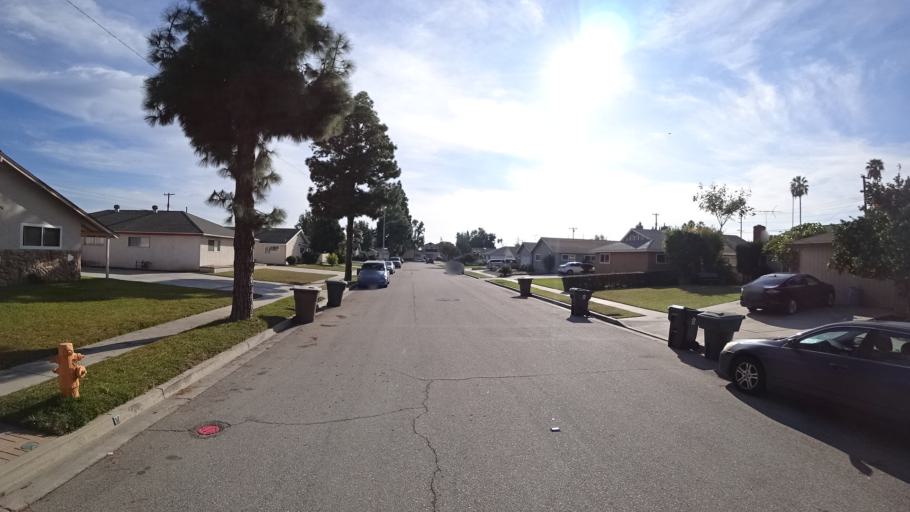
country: US
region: California
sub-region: Orange County
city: Garden Grove
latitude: 33.7795
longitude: -117.9050
